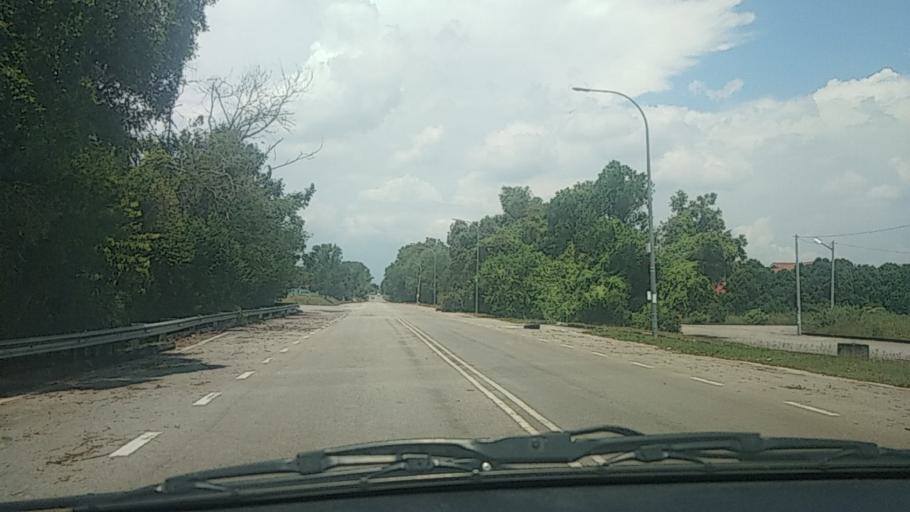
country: MY
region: Kedah
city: Sungai Petani
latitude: 5.6654
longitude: 100.5316
